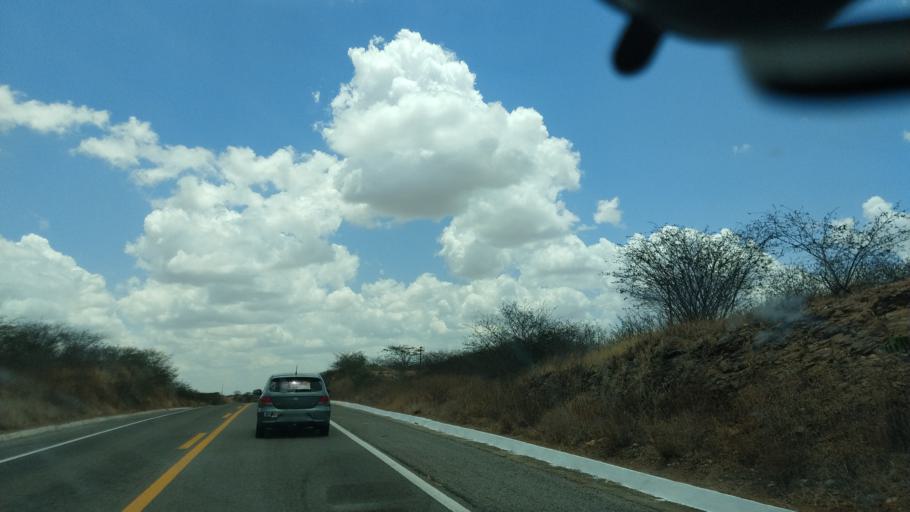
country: BR
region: Rio Grande do Norte
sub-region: Cerro Cora
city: Cerro Cora
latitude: -6.2035
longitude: -36.2770
